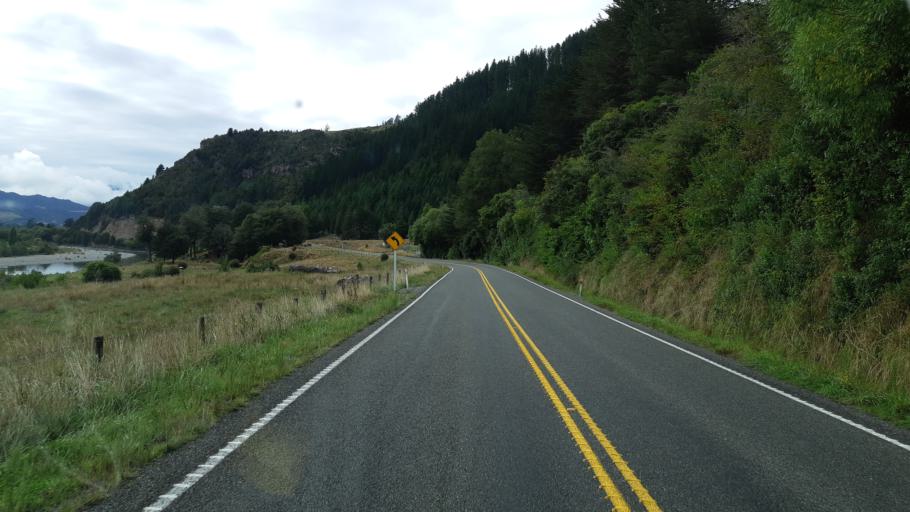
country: NZ
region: West Coast
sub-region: Buller District
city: Westport
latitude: -41.7805
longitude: 172.2595
